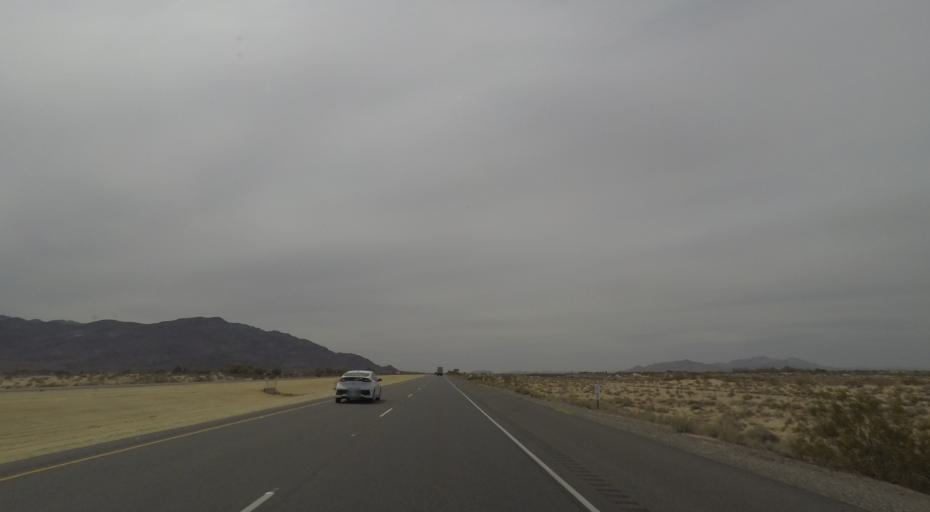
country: US
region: California
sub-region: San Bernardino County
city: Barstow
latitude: 34.8190
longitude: -116.6241
